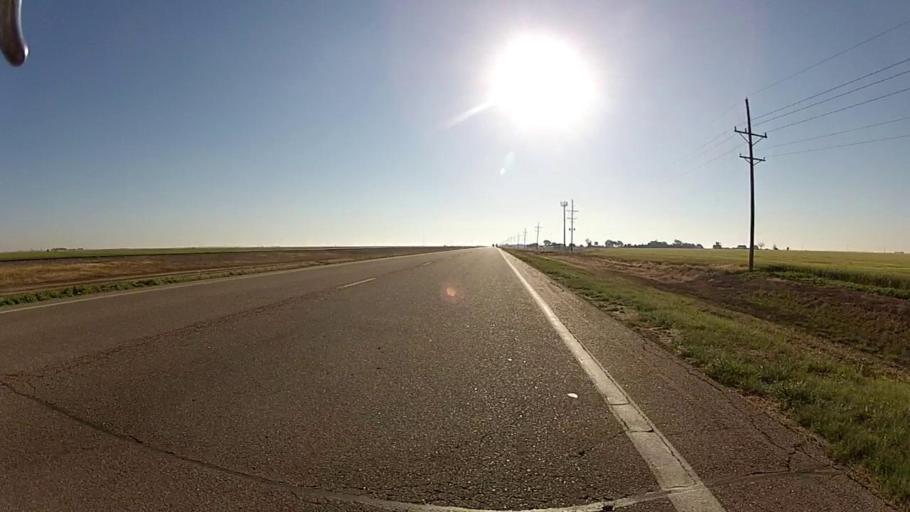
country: US
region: Kansas
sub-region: Haskell County
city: Sublette
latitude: 37.4892
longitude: -100.8232
